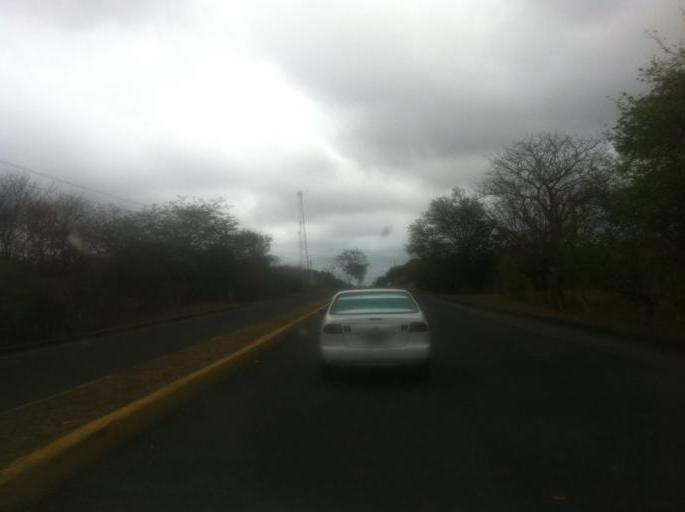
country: NI
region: Granada
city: Granada
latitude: 11.9499
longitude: -85.9847
